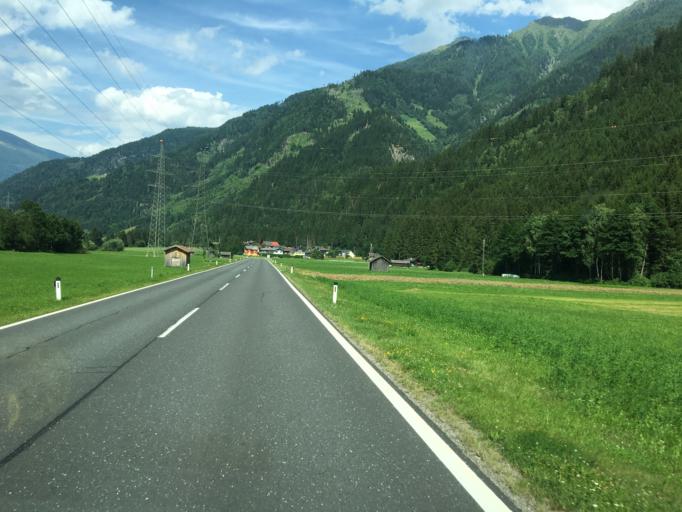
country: AT
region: Carinthia
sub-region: Politischer Bezirk Spittal an der Drau
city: Stall
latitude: 46.8924
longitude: 13.0554
